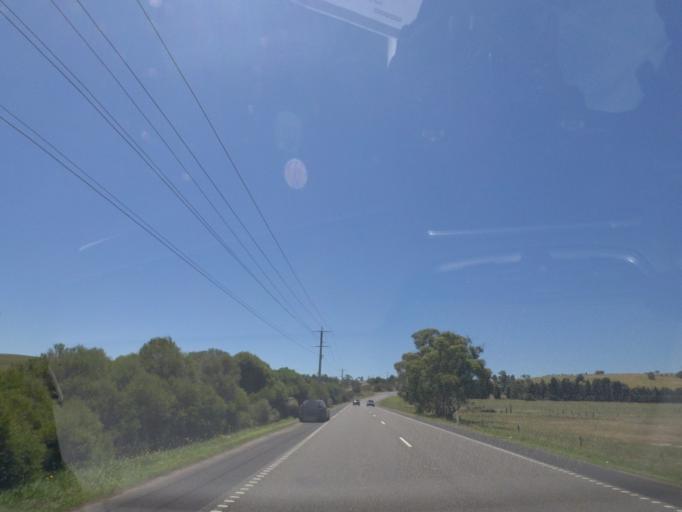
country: AU
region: Victoria
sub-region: Whittlesea
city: Whittlesea
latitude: -37.4618
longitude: 145.0319
